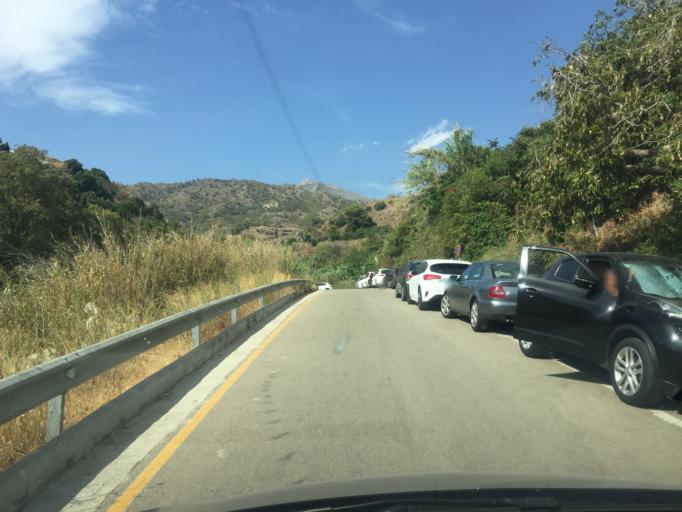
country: ES
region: Andalusia
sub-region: Provincia de Malaga
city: Nerja
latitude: 36.7552
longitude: -3.8350
